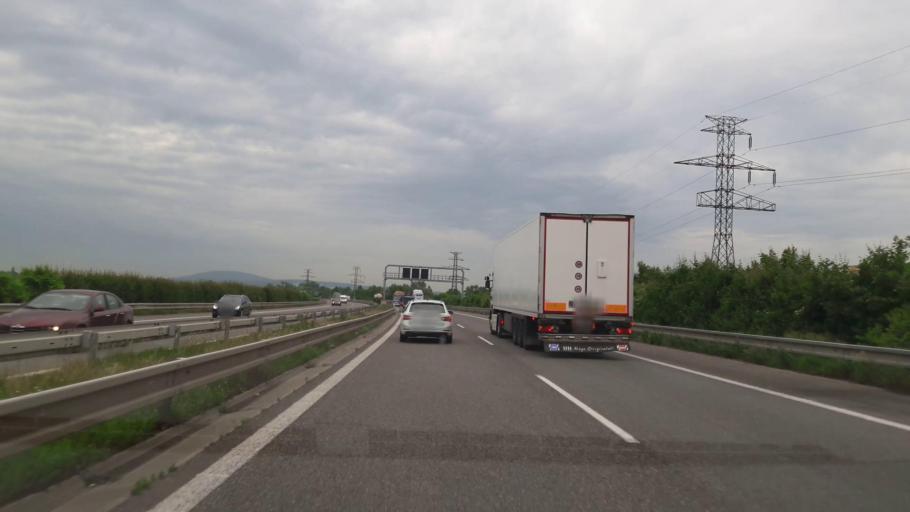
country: AT
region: Burgenland
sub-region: Politischer Bezirk Neusiedl am See
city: Kittsee
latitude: 48.0995
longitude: 17.0972
